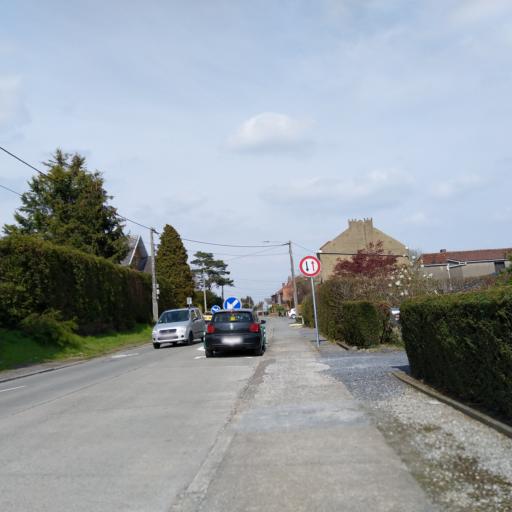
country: BE
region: Wallonia
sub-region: Province du Hainaut
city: Chasse Royale
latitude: 50.4338
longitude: 3.9608
